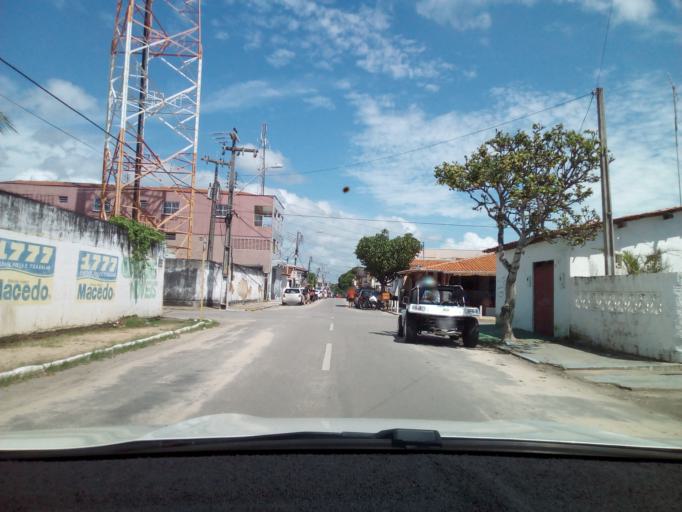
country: BR
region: Ceara
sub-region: Beberibe
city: Beberibe
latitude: -4.1824
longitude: -38.1276
